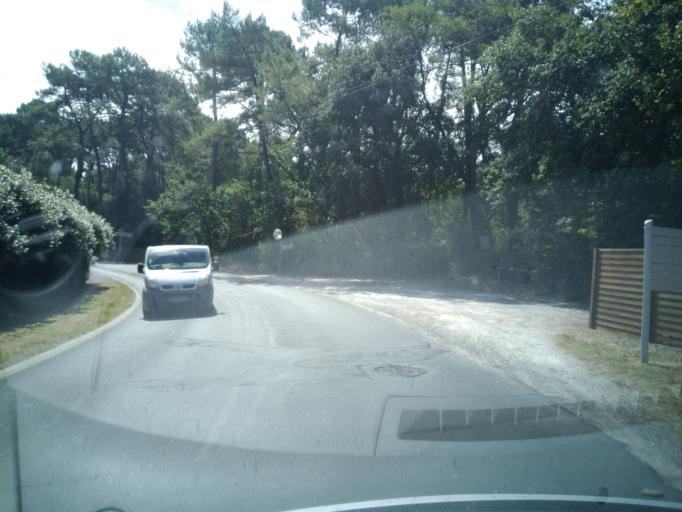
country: FR
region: Poitou-Charentes
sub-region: Departement de la Charente-Maritime
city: Saint-Palais-sur-Mer
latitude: 45.6657
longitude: -1.0789
